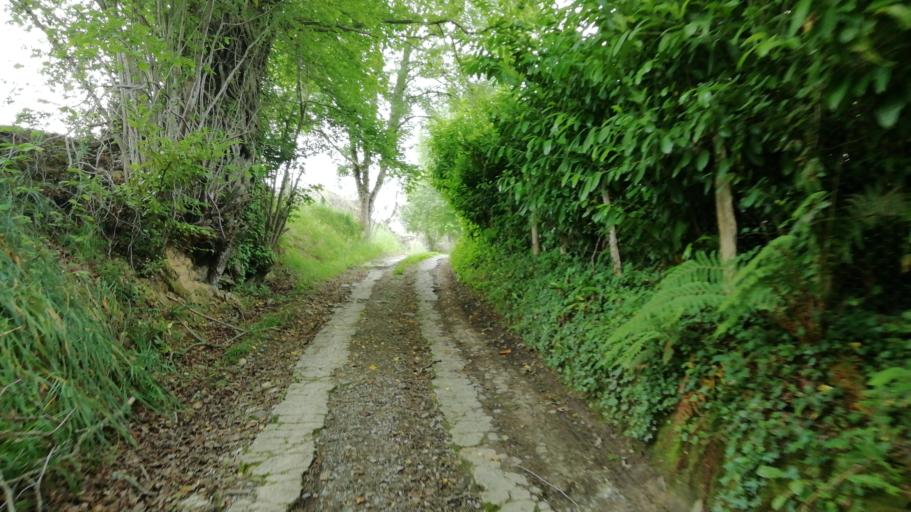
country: FR
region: Aquitaine
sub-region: Departement des Pyrenees-Atlantiques
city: Arudy
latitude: 43.1747
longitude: -0.4258
